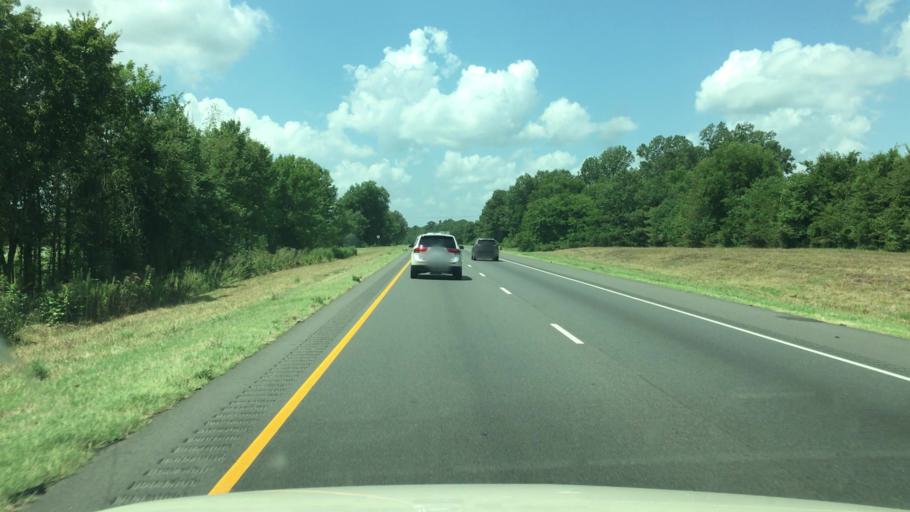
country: US
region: Arkansas
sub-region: Hempstead County
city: Hope
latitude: 33.7222
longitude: -93.5529
